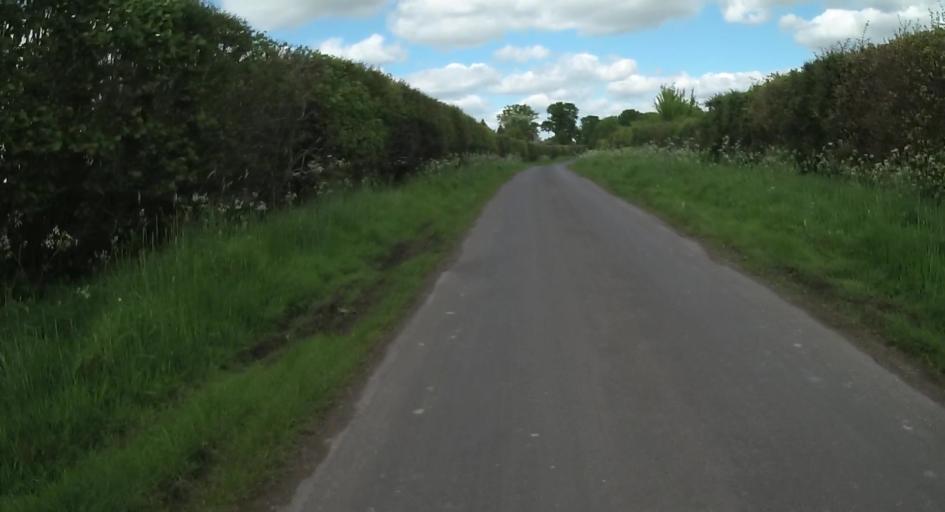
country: GB
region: England
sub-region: West Berkshire
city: Stratfield Mortimer
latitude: 51.3388
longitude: -1.0428
